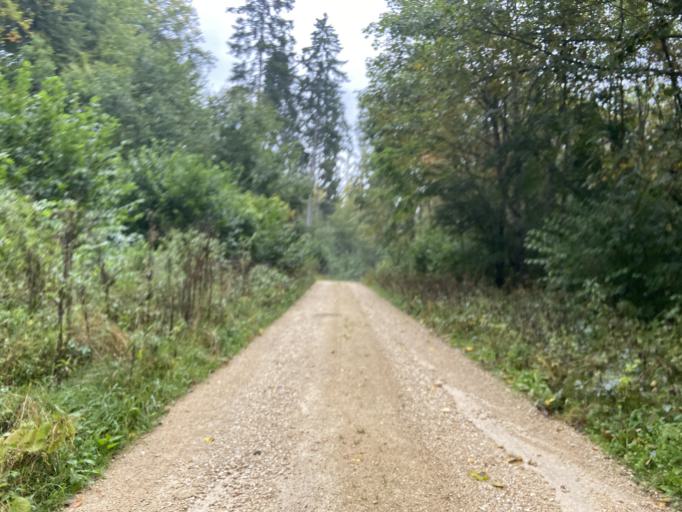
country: DE
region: Baden-Wuerttemberg
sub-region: Tuebingen Region
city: Bingen
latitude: 48.1234
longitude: 9.2715
